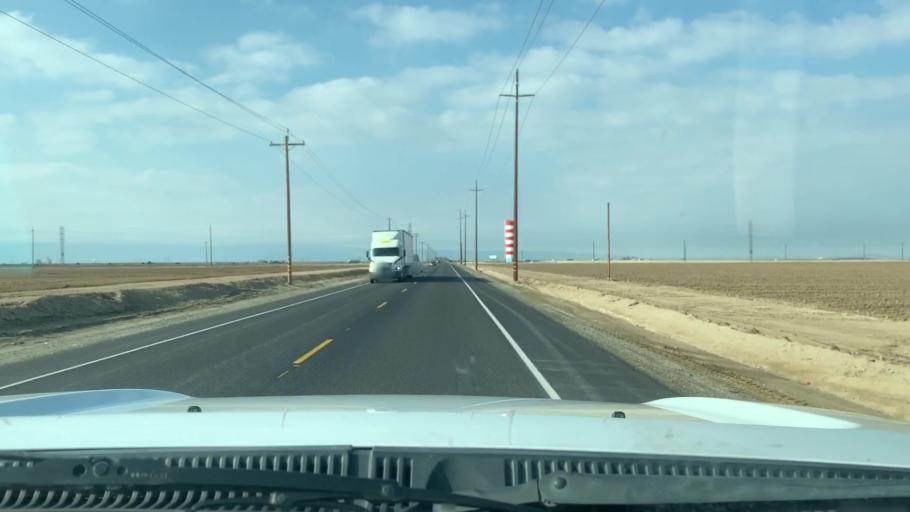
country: US
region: California
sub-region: Kern County
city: Buttonwillow
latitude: 35.4424
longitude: -119.4434
